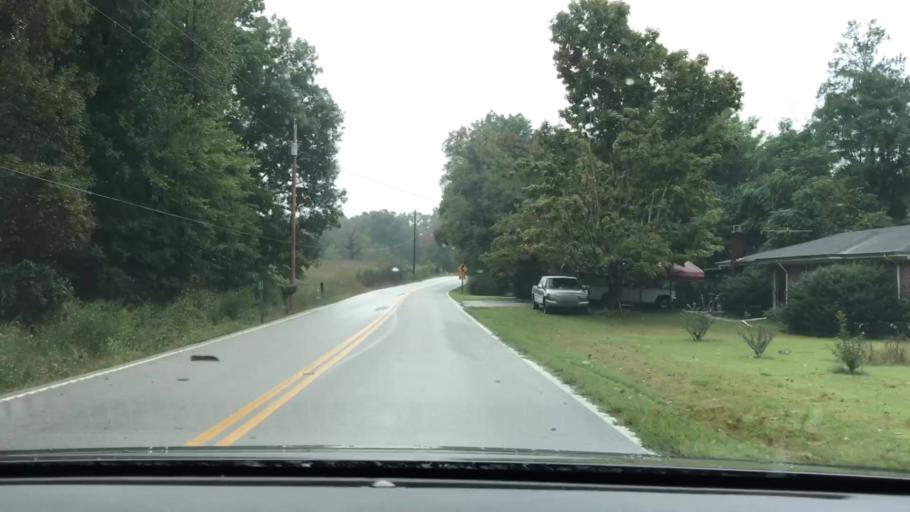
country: US
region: Tennessee
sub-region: Macon County
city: Red Boiling Springs
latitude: 36.4277
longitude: -85.9066
